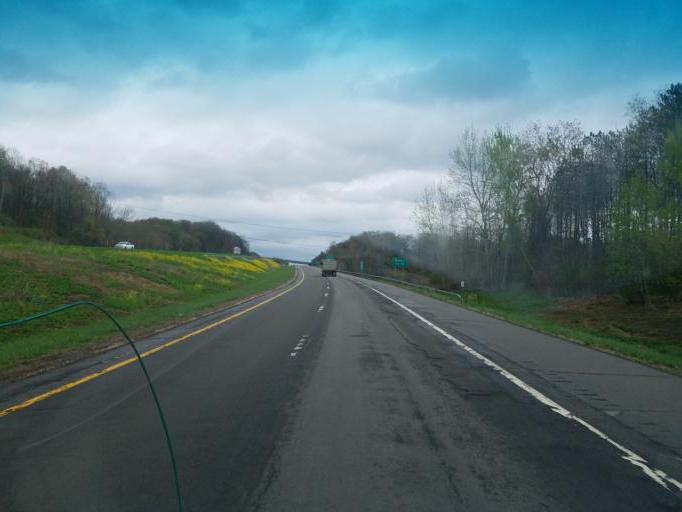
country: US
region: New York
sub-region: Chautauqua County
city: Celoron
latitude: 42.1199
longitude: -79.2553
